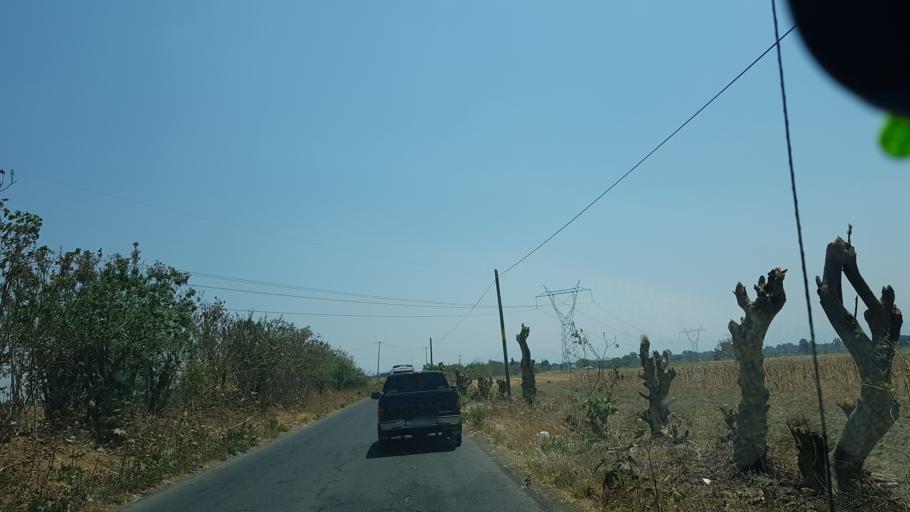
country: MX
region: Puebla
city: Tochimilco
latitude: 18.8893
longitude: -98.5264
